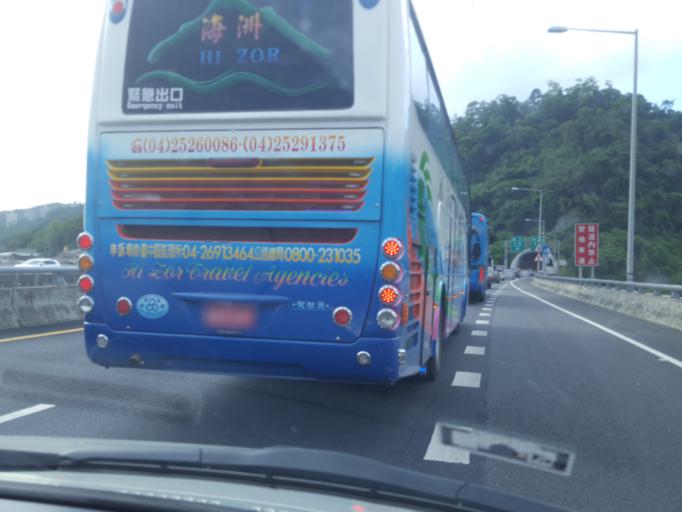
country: TW
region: Taipei
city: Taipei
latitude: 25.0111
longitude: 121.6454
